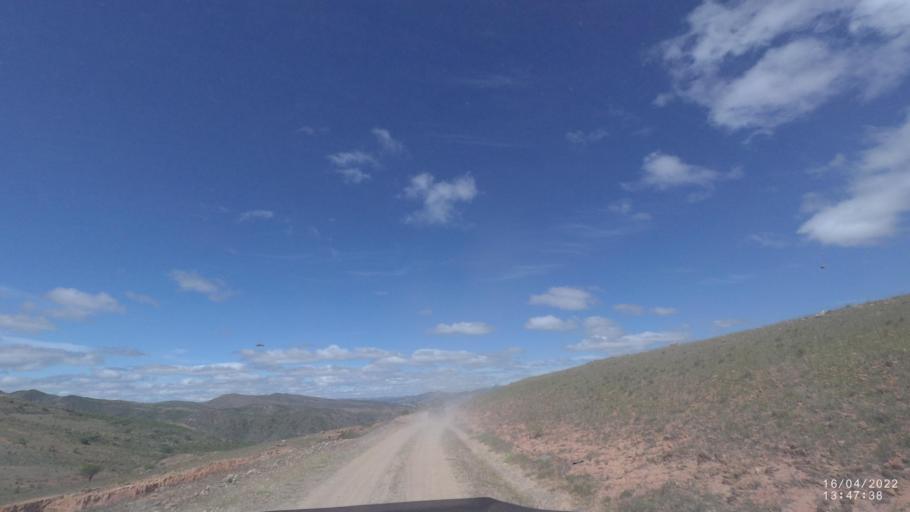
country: BO
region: Cochabamba
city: Mizque
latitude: -18.0094
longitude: -65.5821
